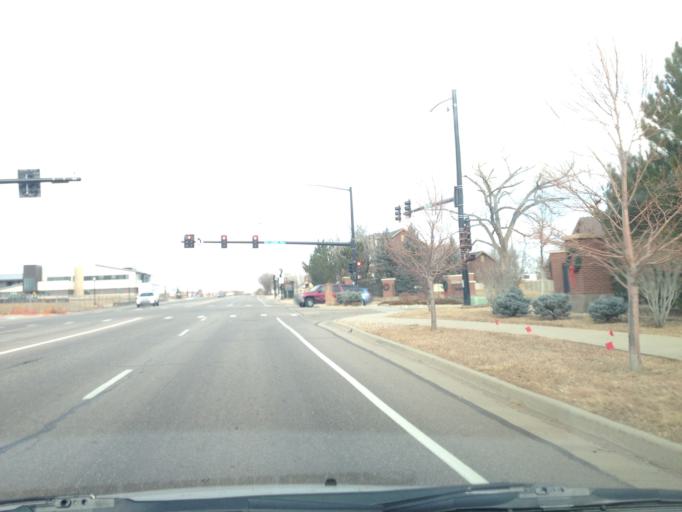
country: US
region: Colorado
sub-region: Boulder County
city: Lafayette
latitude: 39.9808
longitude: -105.0904
